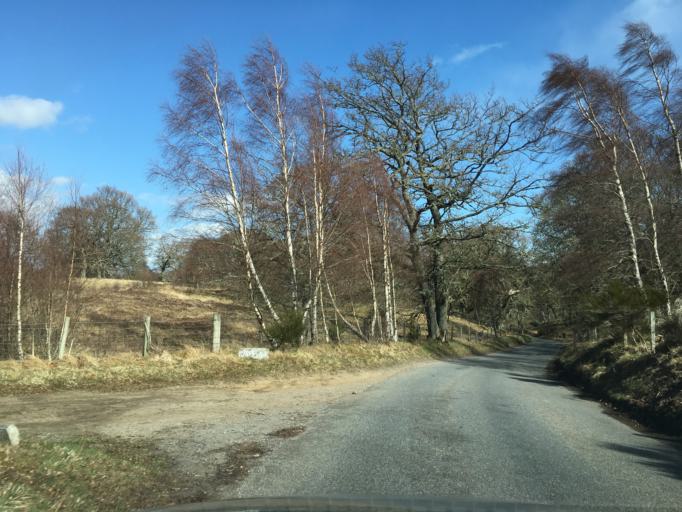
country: GB
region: Scotland
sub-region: Highland
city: Aviemore
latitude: 57.2042
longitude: -3.7930
